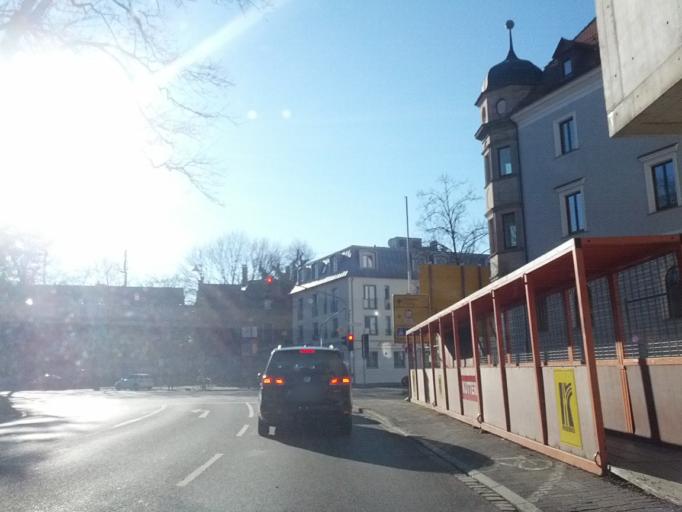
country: DE
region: Bavaria
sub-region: Swabia
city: Memmingen
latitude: 47.9863
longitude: 10.1765
